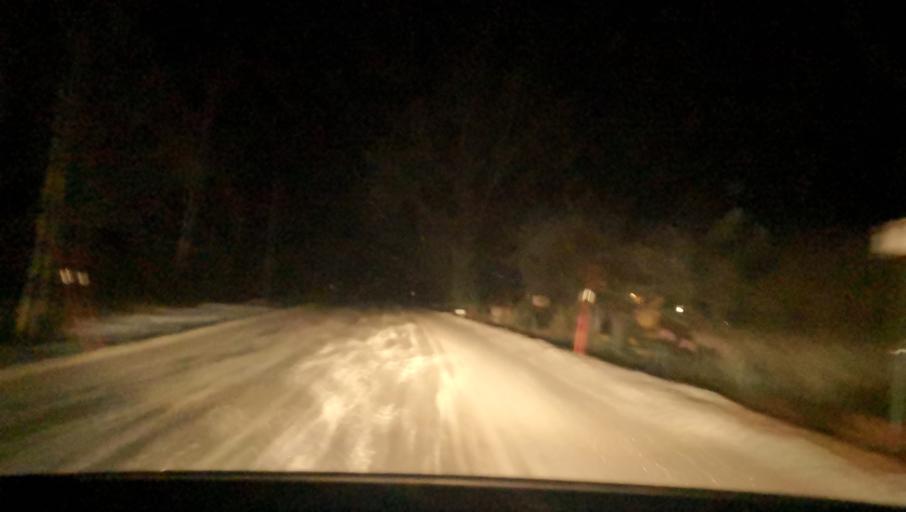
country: SE
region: Uppsala
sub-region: Heby Kommun
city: Tarnsjo
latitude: 60.1393
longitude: 16.9058
